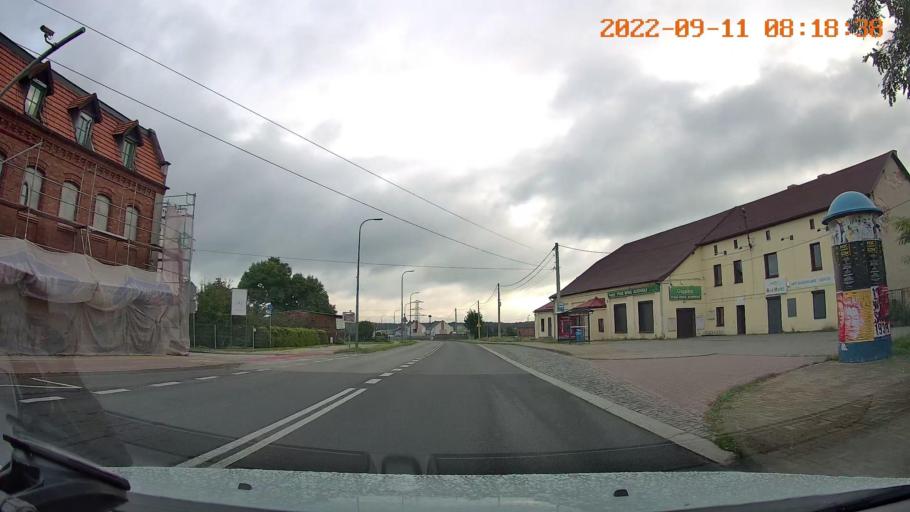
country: PL
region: Silesian Voivodeship
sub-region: Tychy
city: Tychy
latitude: 50.1464
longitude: 18.9998
